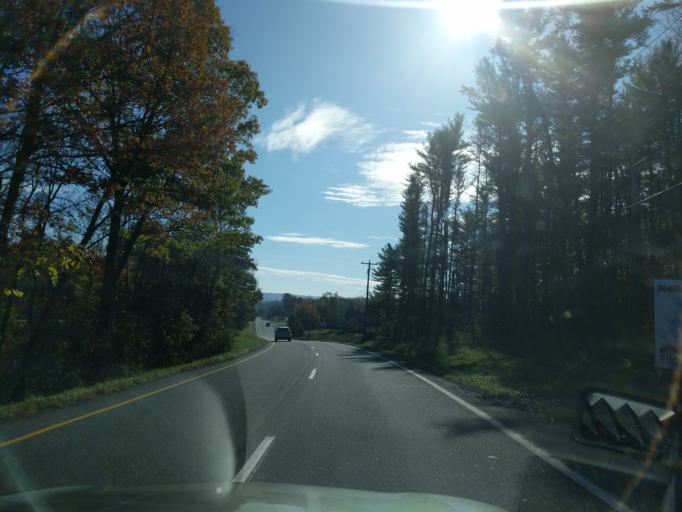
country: US
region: Virginia
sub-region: Frederick County
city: Shawnee Land
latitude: 39.2946
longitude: -78.2764
